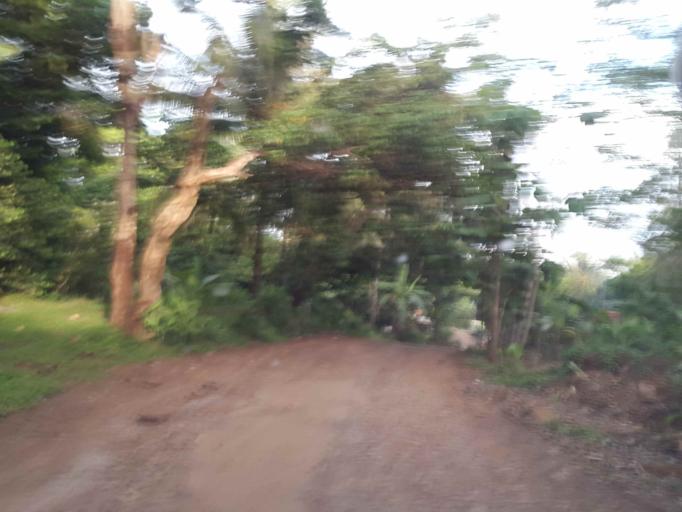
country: ID
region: Banten
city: Marapat
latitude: -6.6016
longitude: 105.6990
